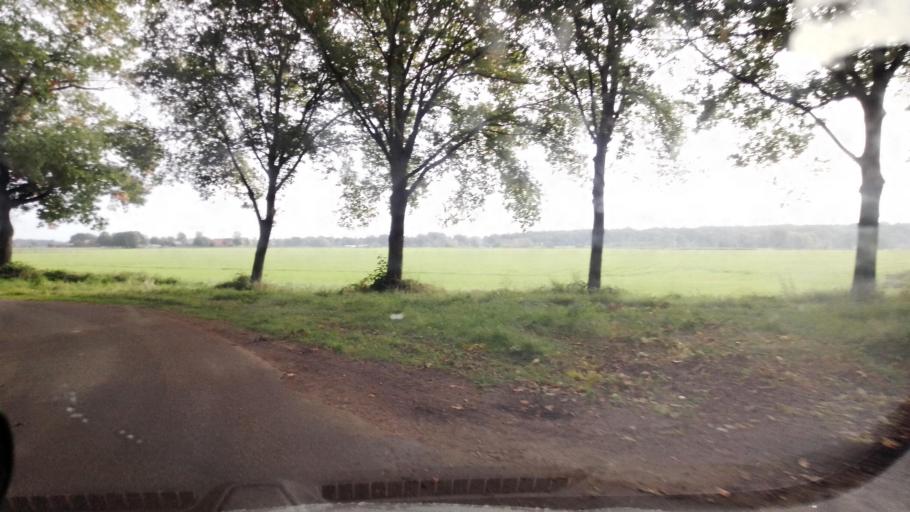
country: NL
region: Limburg
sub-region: Gemeente Beesel
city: Reuver
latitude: 51.3068
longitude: 6.0879
